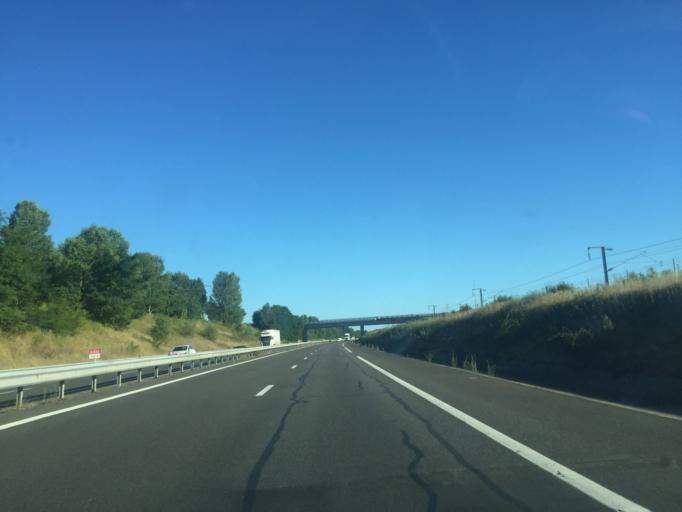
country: FR
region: Rhone-Alpes
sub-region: Departement du Rhone
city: Jons
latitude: 45.8033
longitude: 5.0701
